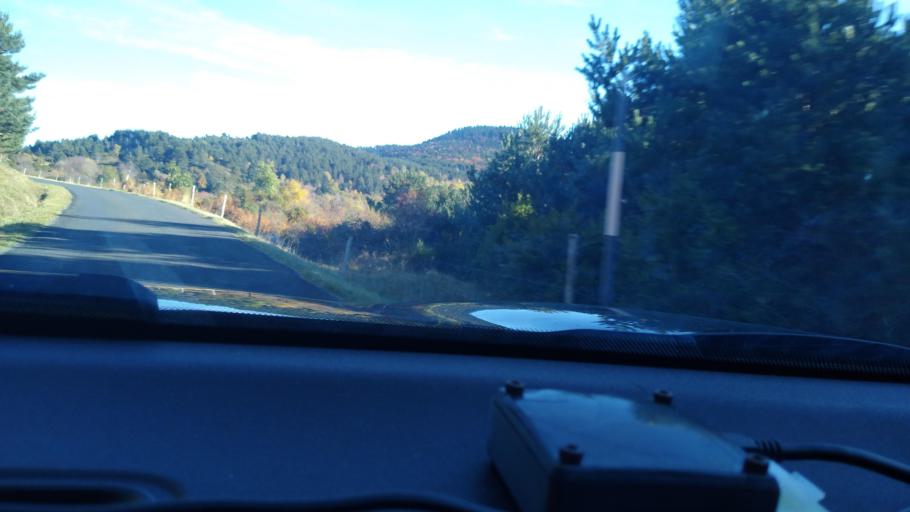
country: FR
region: Languedoc-Roussillon
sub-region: Departement de l'Aude
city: Quillan
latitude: 42.7386
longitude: 2.1442
